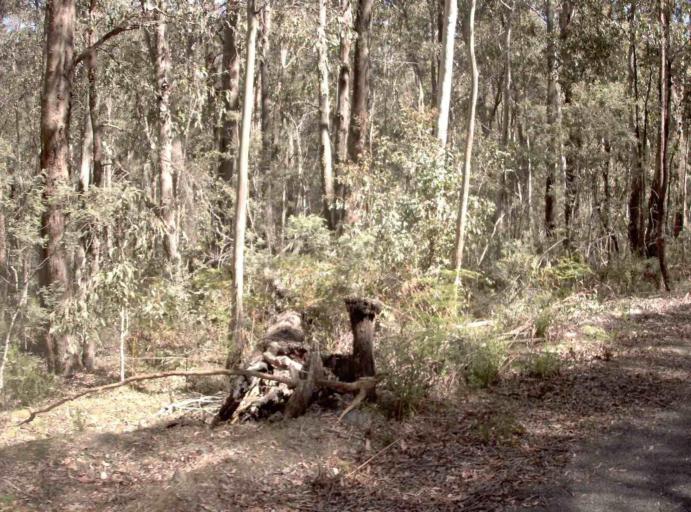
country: AU
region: New South Wales
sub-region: Bombala
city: Bombala
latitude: -37.1228
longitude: 148.7503
